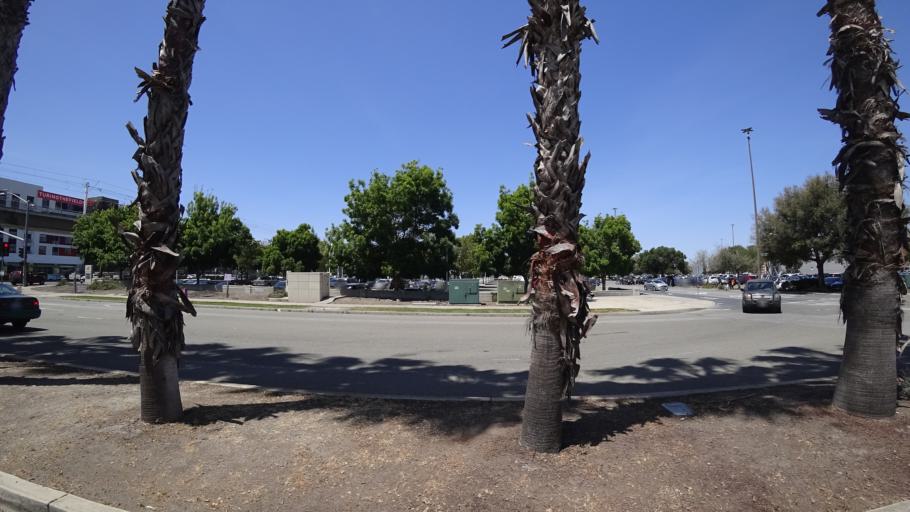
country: US
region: California
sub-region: Santa Clara County
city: Milpitas
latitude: 37.4131
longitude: -121.8984
